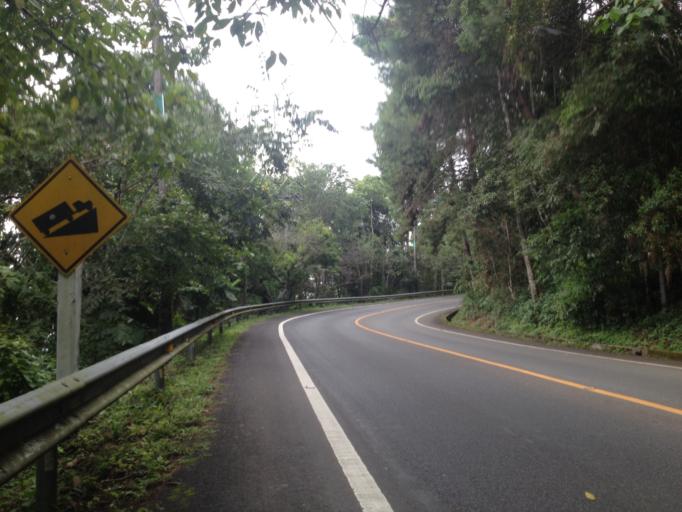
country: TH
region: Chiang Mai
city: Chiang Mai
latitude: 18.8020
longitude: 98.8993
